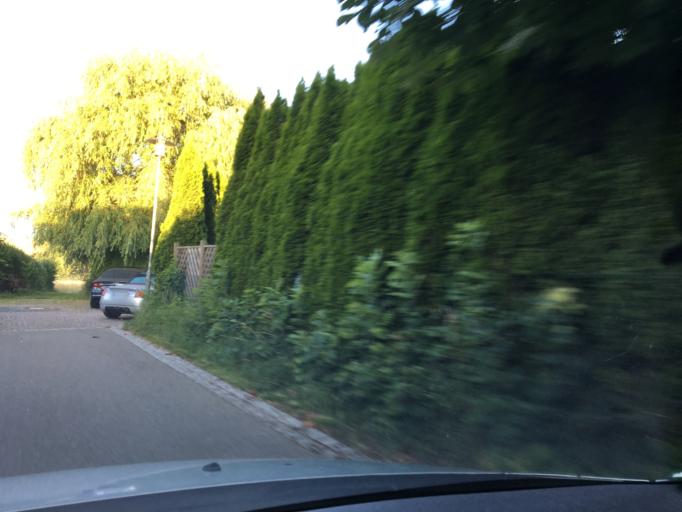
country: DE
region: Bavaria
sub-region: Upper Bavaria
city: Haimhausen
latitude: 48.3102
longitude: 11.5498
